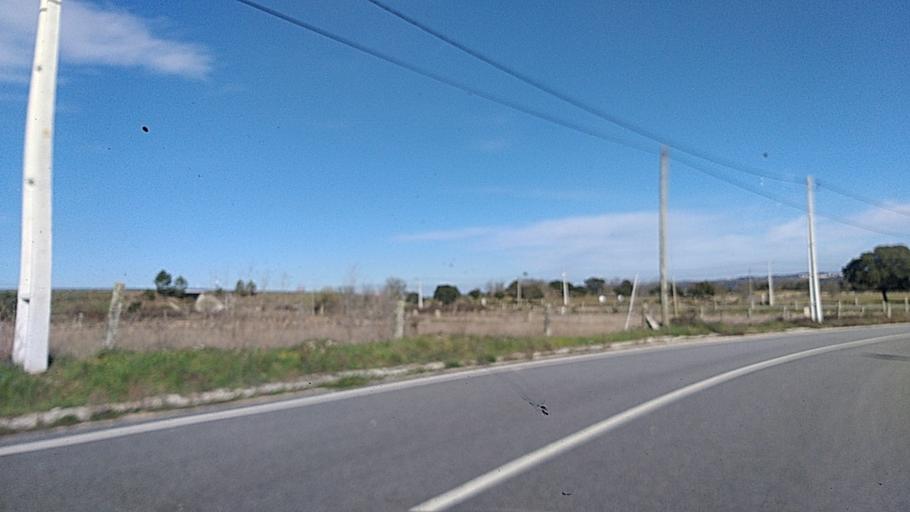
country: ES
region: Castille and Leon
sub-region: Provincia de Salamanca
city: Fuentes de Onoro
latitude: 40.6027
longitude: -6.9490
